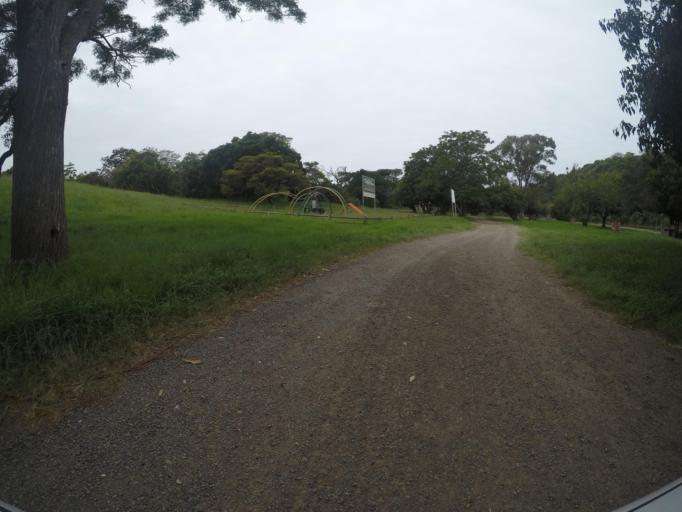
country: ZA
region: Eastern Cape
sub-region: Buffalo City Metropolitan Municipality
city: East London
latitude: -32.9745
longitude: 27.9268
